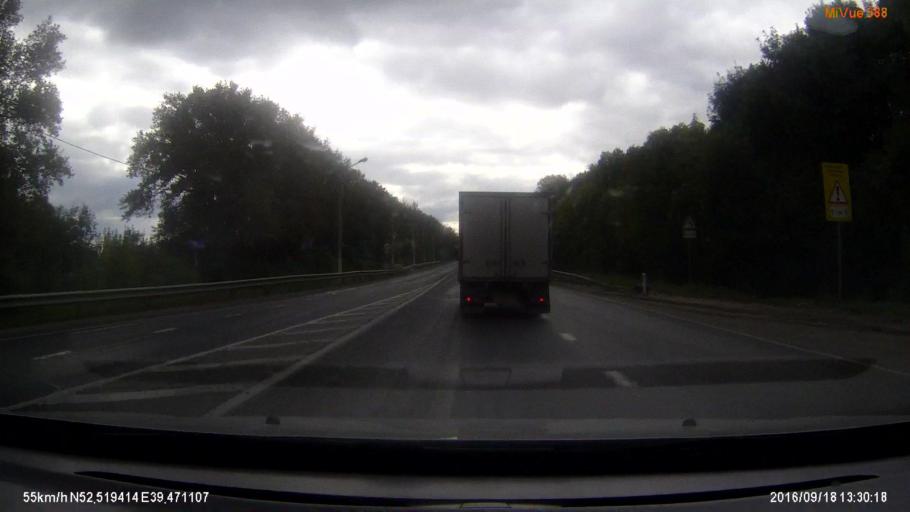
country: RU
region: Lipetsk
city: Borinskoye
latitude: 52.4703
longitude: 39.4197
